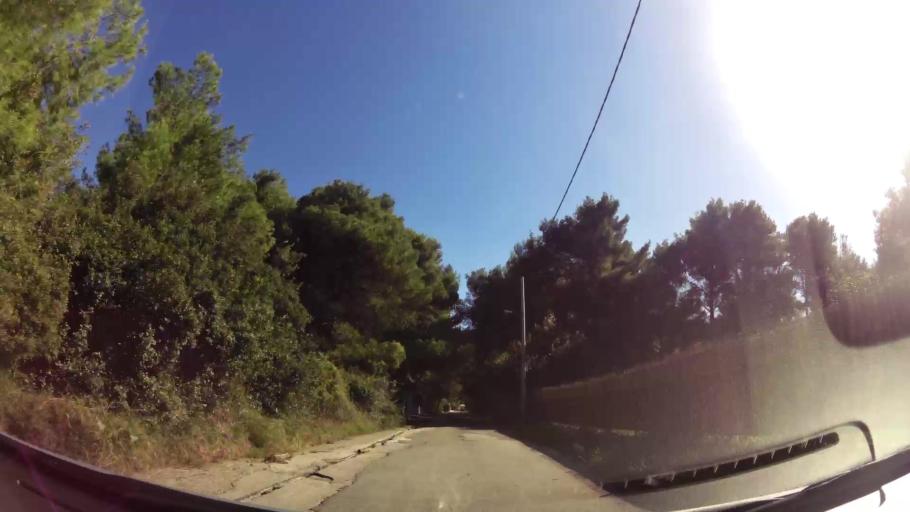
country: GR
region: Attica
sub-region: Nomarchia Athinas
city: Ekali
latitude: 38.1066
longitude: 23.8286
